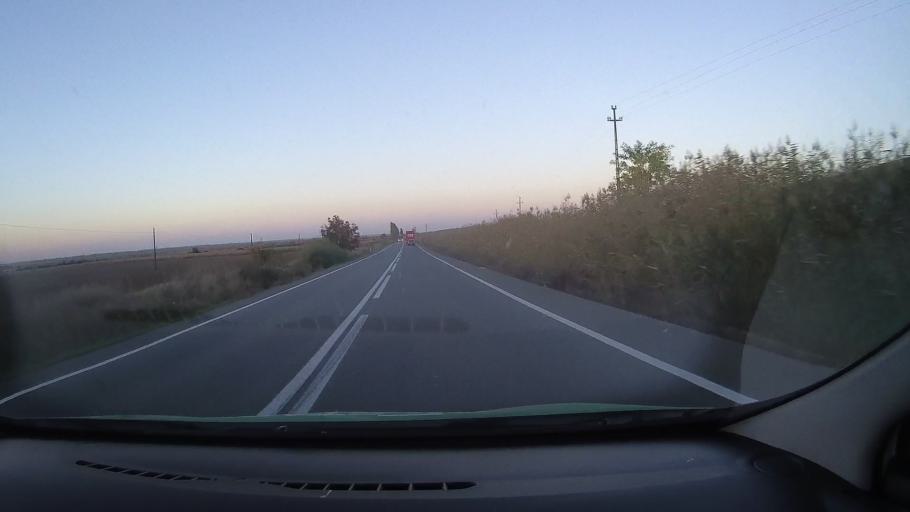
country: RO
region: Bihor
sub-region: Comuna Cherechiu
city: Cherechiu
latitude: 47.3841
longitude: 22.1438
